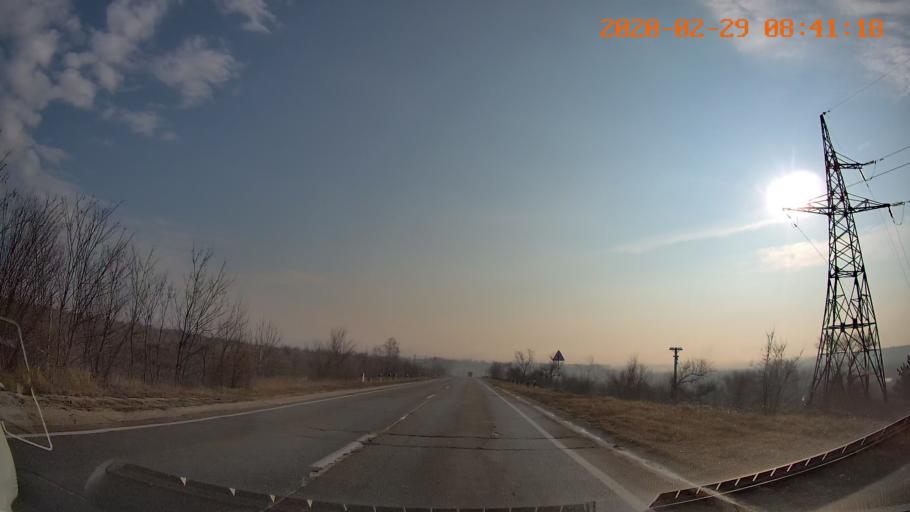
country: MD
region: Anenii Noi
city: Varnita
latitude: 46.9240
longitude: 29.4341
